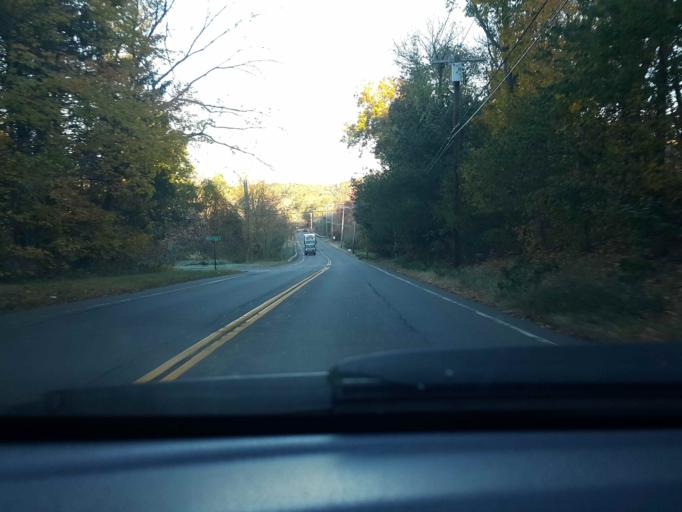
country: US
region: Connecticut
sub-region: New Haven County
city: Woodbridge
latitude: 41.3806
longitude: -73.0110
